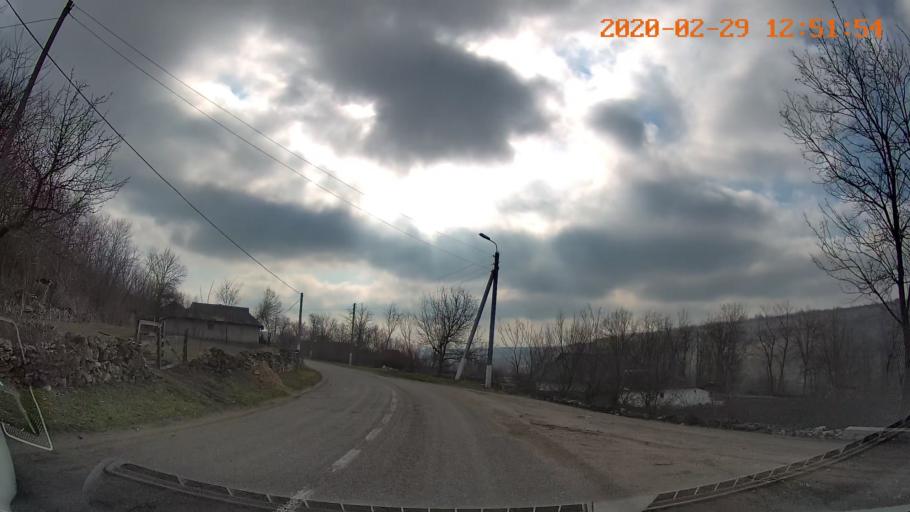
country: MD
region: Telenesti
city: Camenca
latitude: 48.1161
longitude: 28.7319
